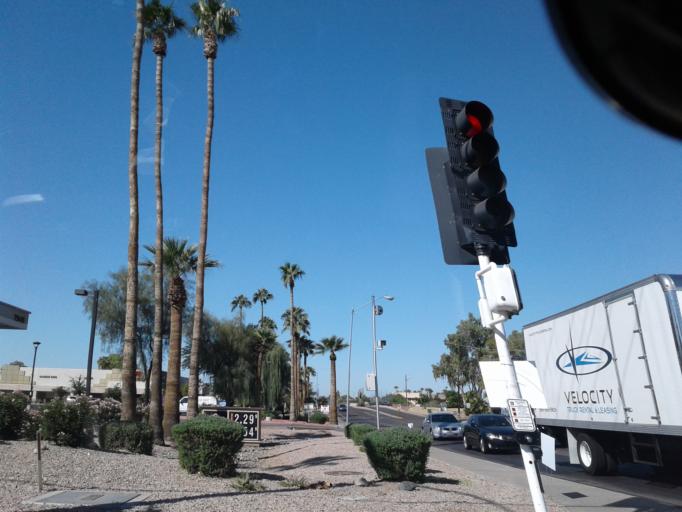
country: US
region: Arizona
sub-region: Maricopa County
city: Scottsdale
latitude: 33.4804
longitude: -111.9091
